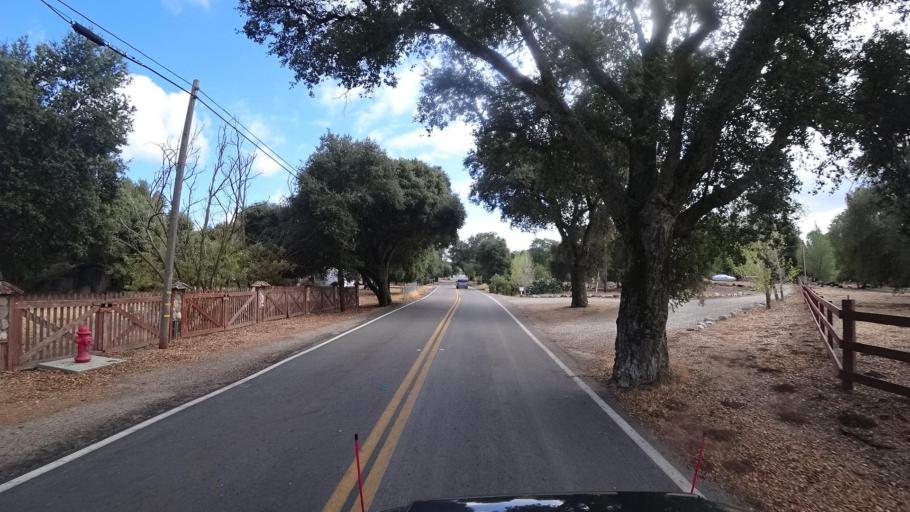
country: US
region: California
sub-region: San Diego County
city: Campo
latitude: 32.6818
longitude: -116.5147
